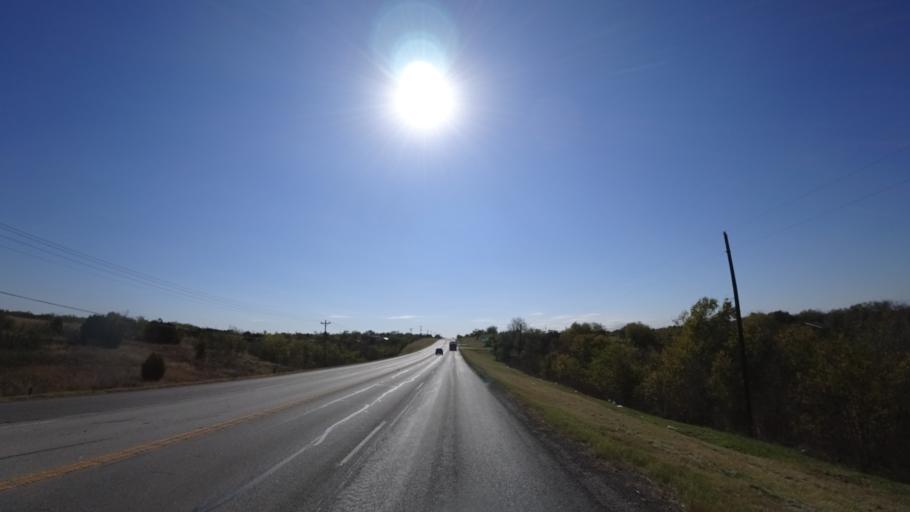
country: US
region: Texas
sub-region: Travis County
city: Onion Creek
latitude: 30.1234
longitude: -97.6956
